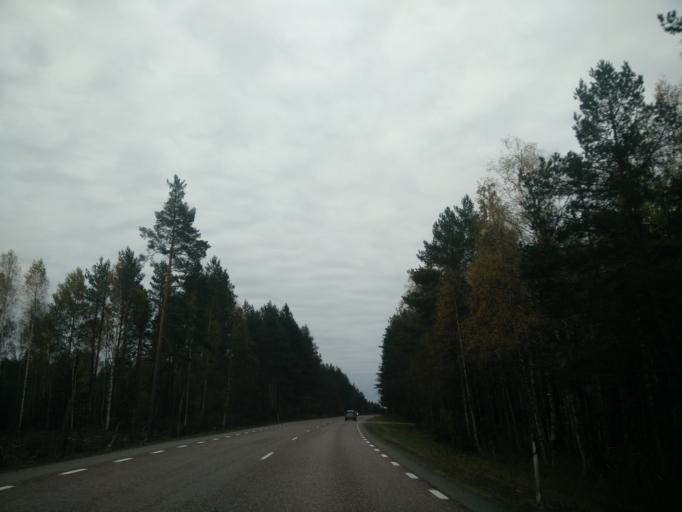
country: SE
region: Gaevleborg
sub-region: Gavle Kommun
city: Norrsundet
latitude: 60.8330
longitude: 17.2073
